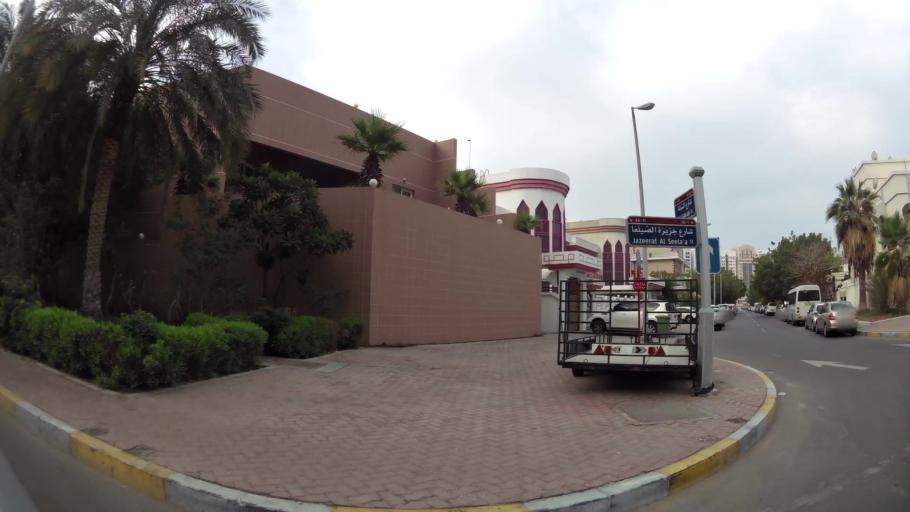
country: AE
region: Abu Dhabi
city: Abu Dhabi
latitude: 24.4745
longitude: 54.3726
